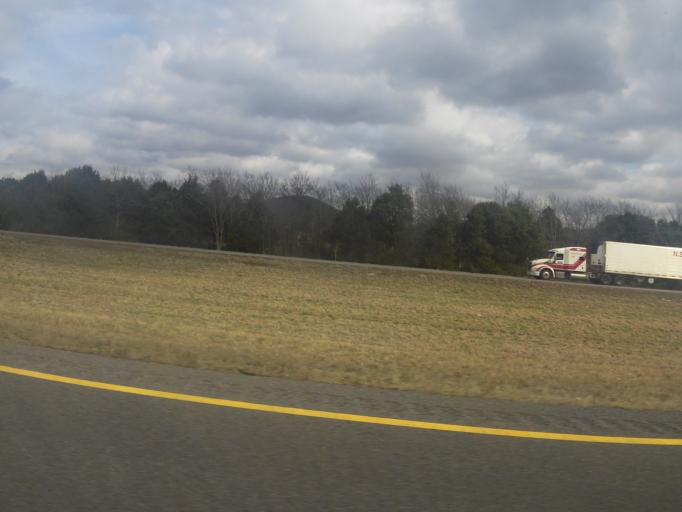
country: US
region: Tennessee
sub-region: Rutherford County
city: Plainview
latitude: 35.6817
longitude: -86.2895
